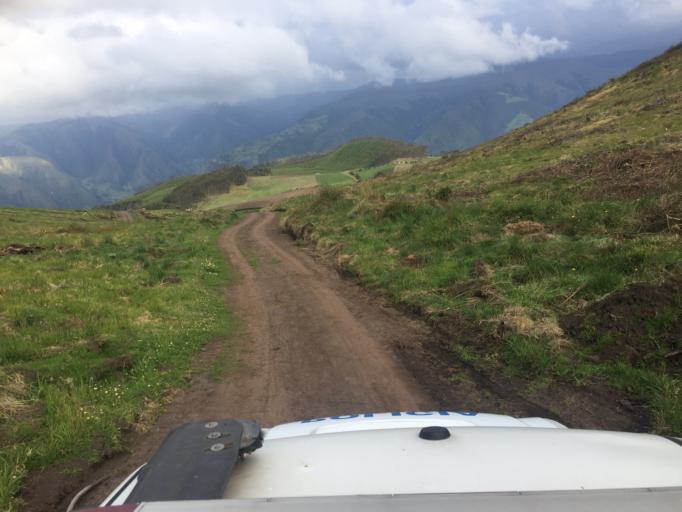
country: EC
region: Imbabura
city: Ibarra
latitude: 0.2250
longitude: -78.1240
